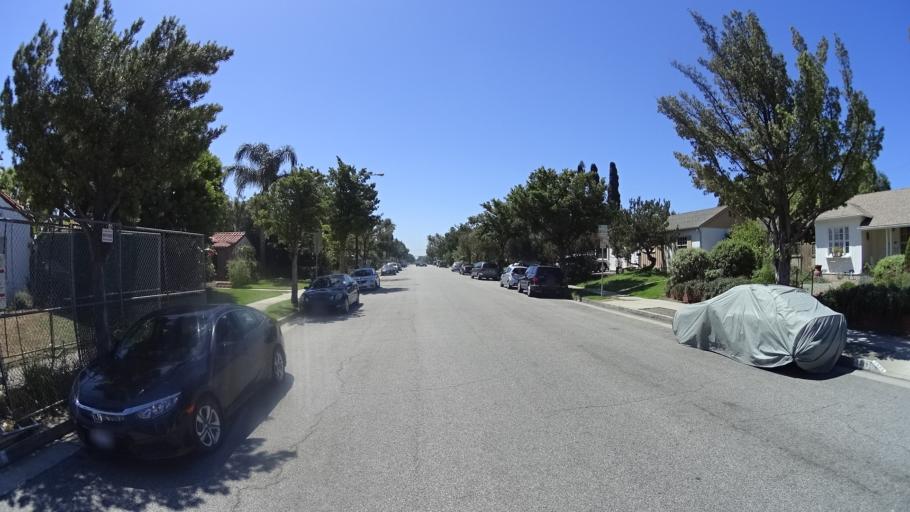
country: US
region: California
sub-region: Los Angeles County
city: Santa Monica
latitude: 34.0246
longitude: -118.4579
